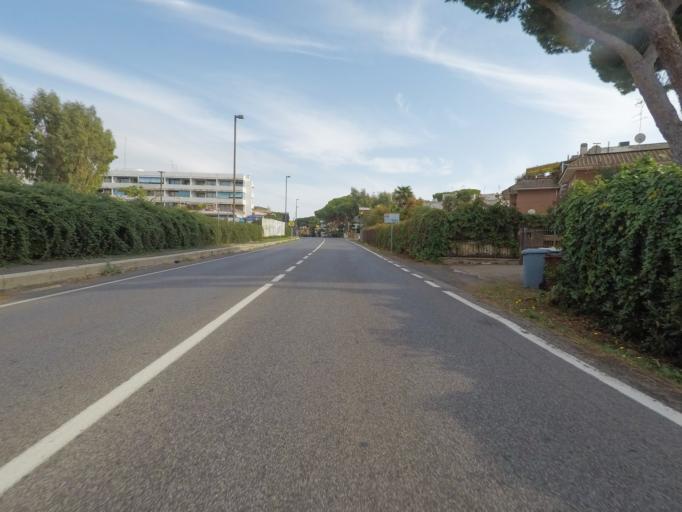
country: IT
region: Latium
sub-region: Citta metropolitana di Roma Capitale
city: Santa Marinella
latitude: 42.0337
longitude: 11.8361
